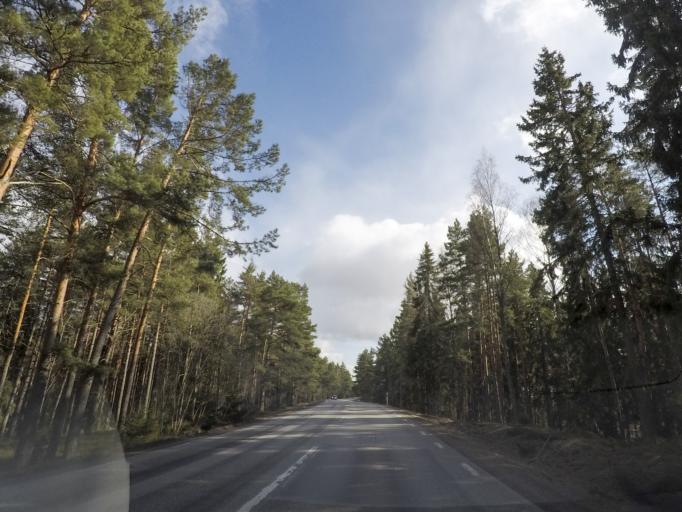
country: SE
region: Vaestmanland
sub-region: Hallstahammars Kommun
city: Hallstahammar
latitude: 59.6489
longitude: 16.1887
